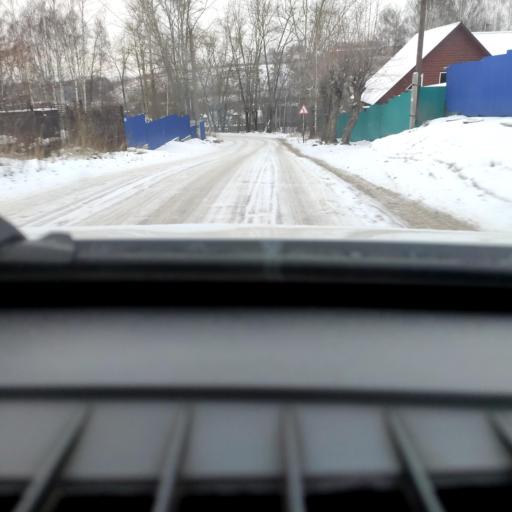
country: RU
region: Perm
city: Perm
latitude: 58.1033
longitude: 56.3659
